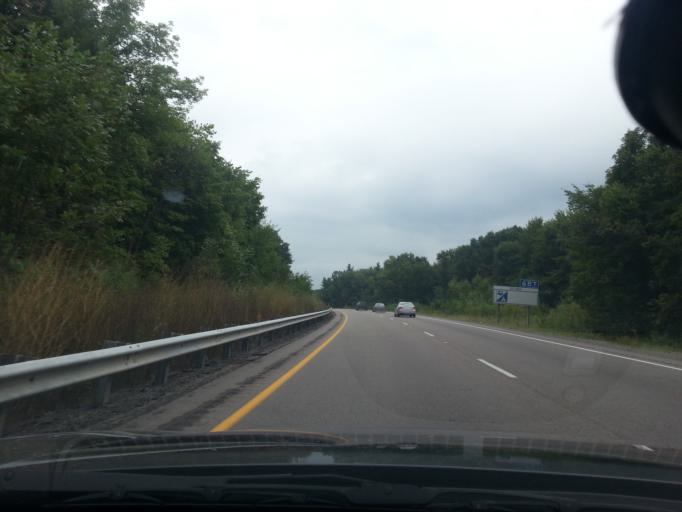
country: CA
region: Ontario
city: Brockville
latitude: 44.5186
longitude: -75.7910
